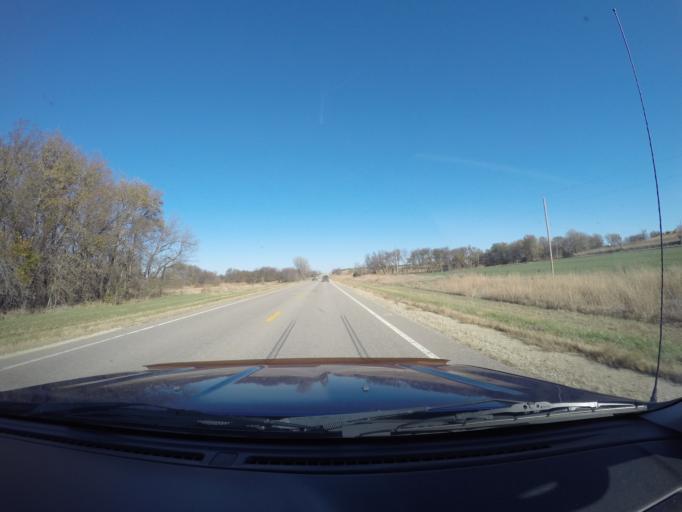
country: US
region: Kansas
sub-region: Riley County
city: Ogden
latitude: 39.3234
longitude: -96.7559
